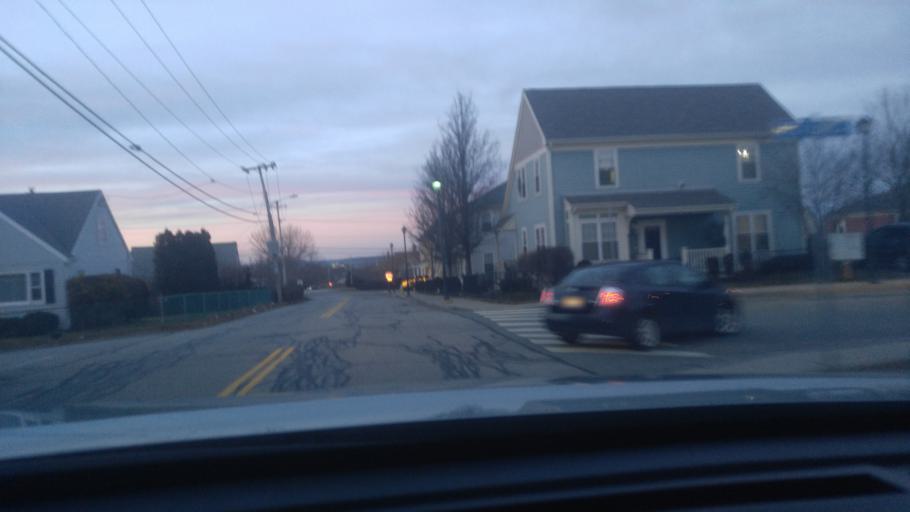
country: US
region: Rhode Island
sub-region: Newport County
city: Newport
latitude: 41.5149
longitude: -71.3138
